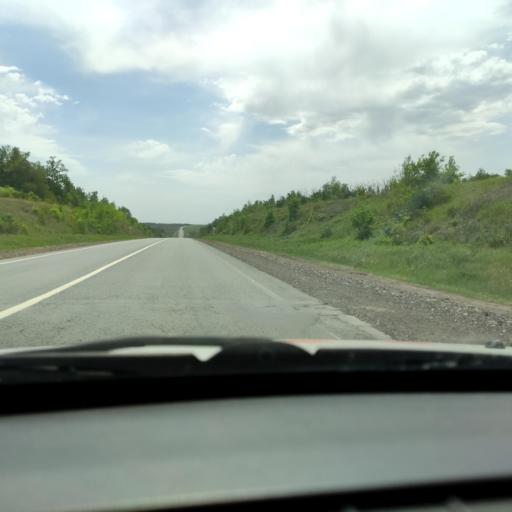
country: RU
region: Samara
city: Yelkhovka
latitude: 53.7065
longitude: 50.2275
